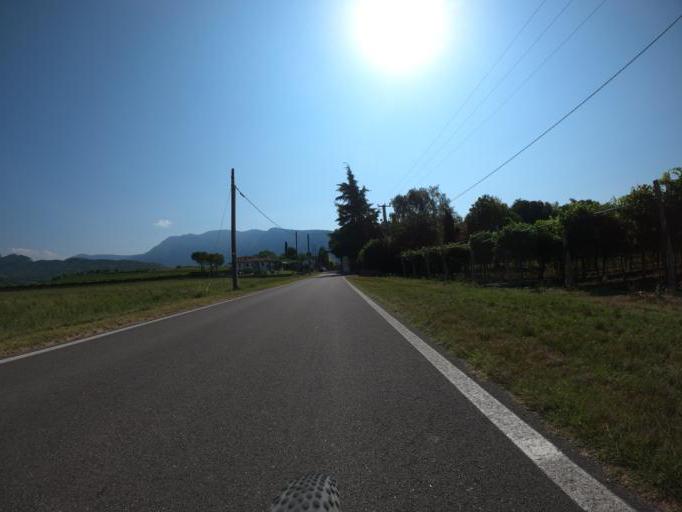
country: IT
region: Veneto
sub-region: Provincia di Verona
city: Rivoli Veronese
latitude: 45.5839
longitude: 10.8006
